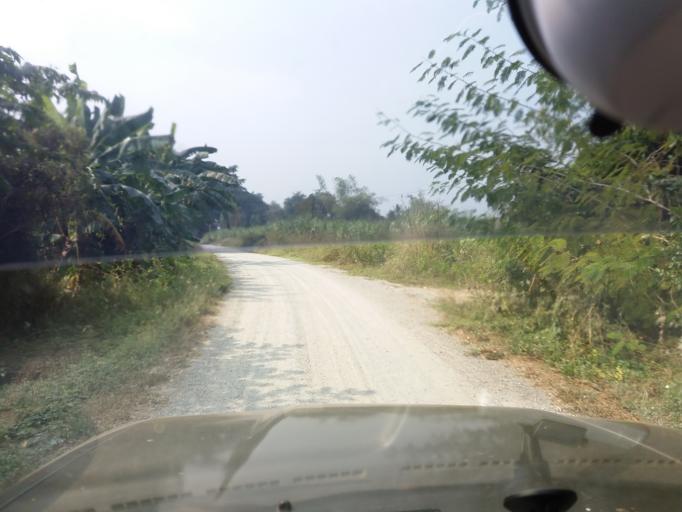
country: TH
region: Sing Buri
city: Bang Racham
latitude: 14.8973
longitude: 100.2075
